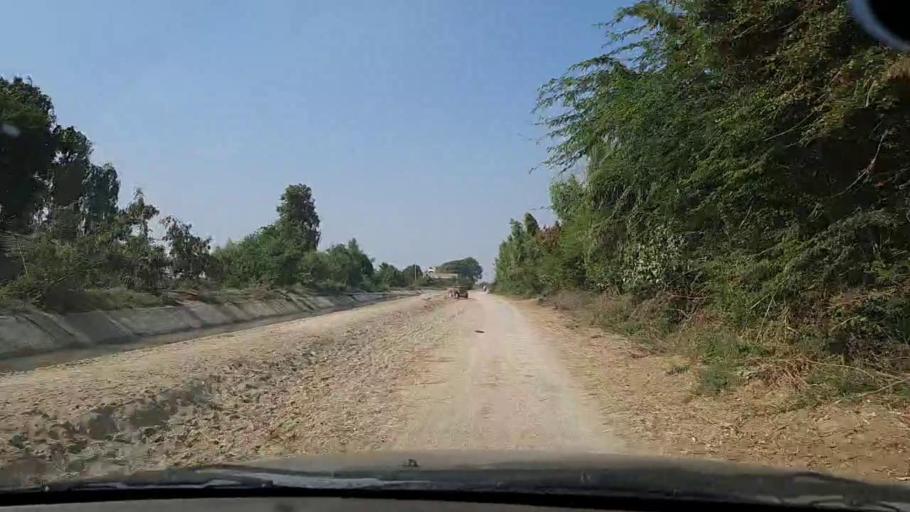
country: PK
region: Sindh
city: Chuhar Jamali
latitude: 24.4255
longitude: 67.8152
